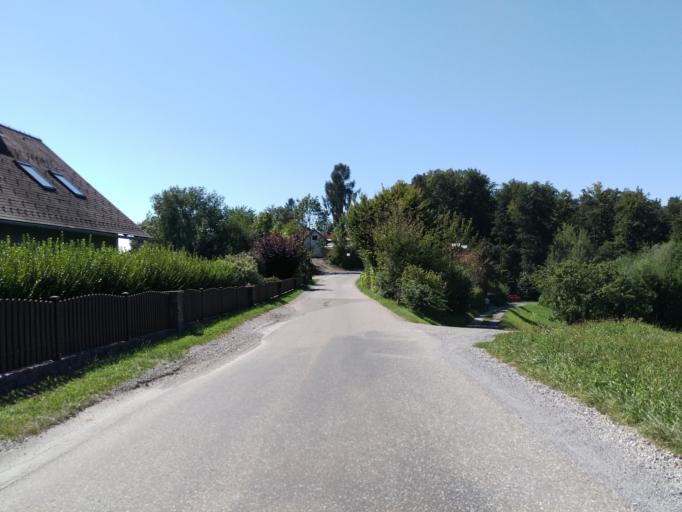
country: AT
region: Styria
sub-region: Politischer Bezirk Graz-Umgebung
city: Eggersdorf bei Graz
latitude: 47.0831
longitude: 15.5601
